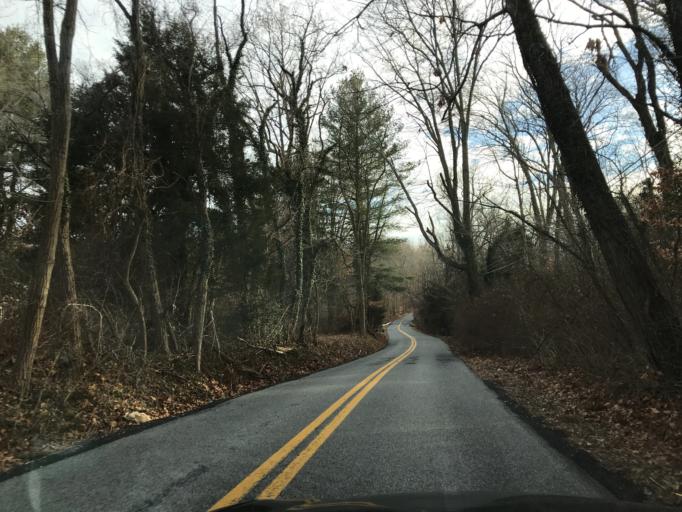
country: US
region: Maryland
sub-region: Baltimore County
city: Kingsville
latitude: 39.4451
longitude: -76.4022
